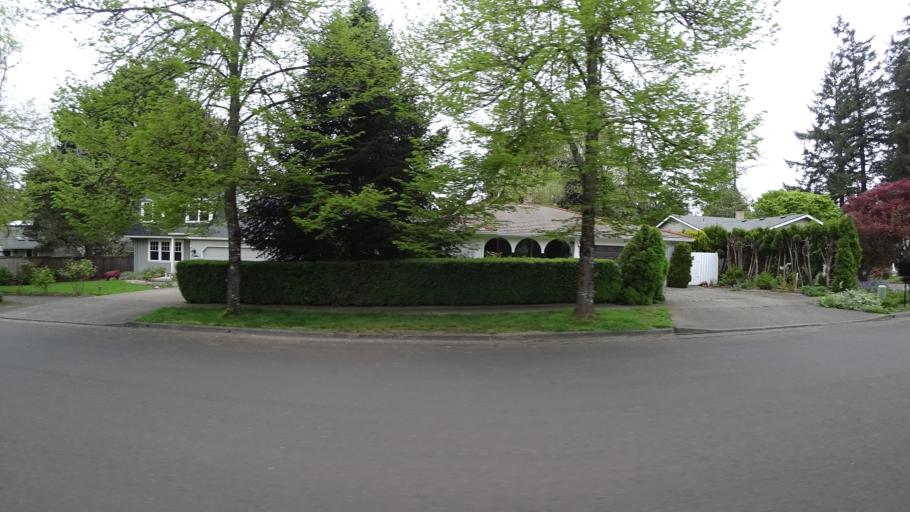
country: US
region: Oregon
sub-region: Washington County
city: Beaverton
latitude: 45.4640
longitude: -122.8290
